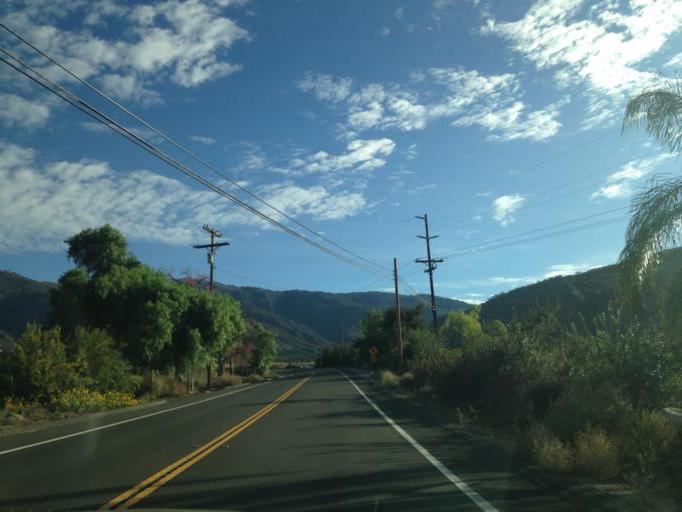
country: US
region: California
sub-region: San Diego County
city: Valley Center
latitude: 33.2955
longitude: -116.9454
